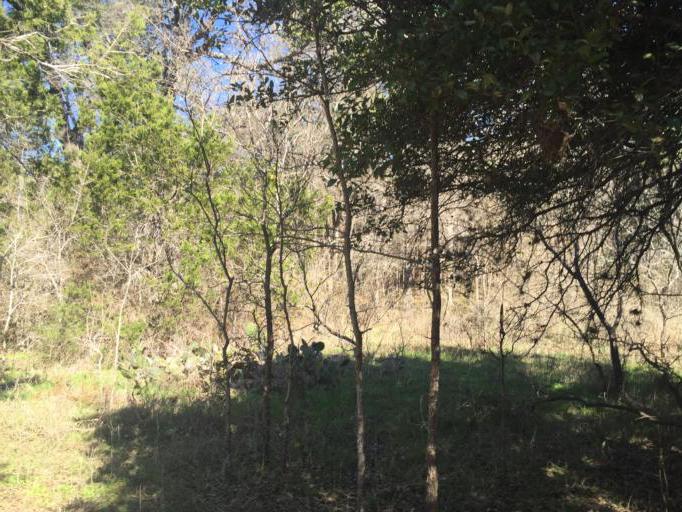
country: US
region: Texas
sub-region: Travis County
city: Onion Creek
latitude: 30.1578
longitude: -97.8057
